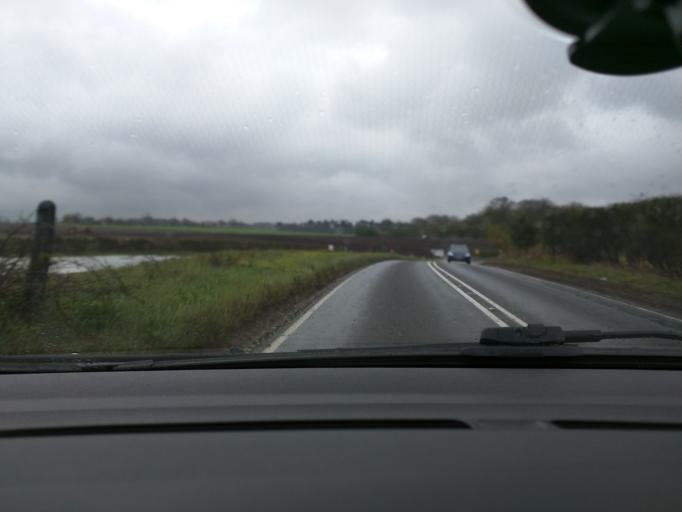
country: GB
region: England
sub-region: Suffolk
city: Leiston
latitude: 52.1805
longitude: 1.5336
